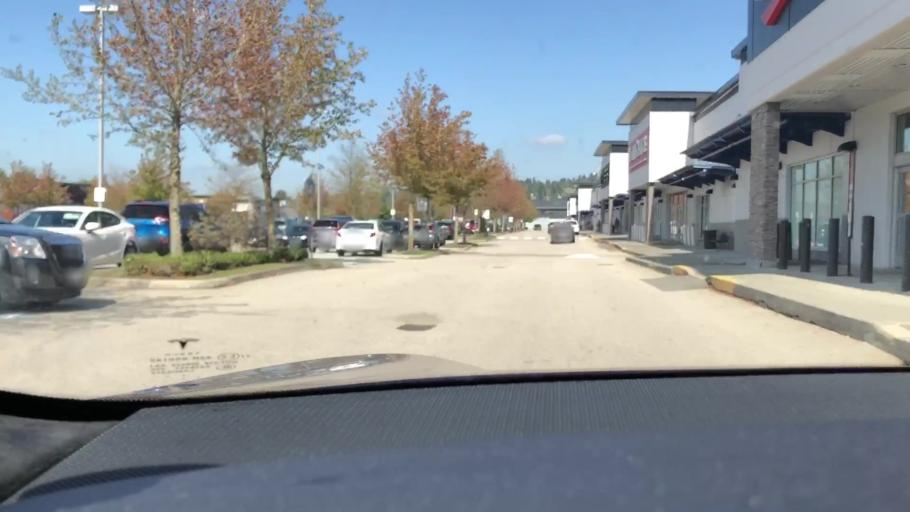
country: CA
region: British Columbia
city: New Westminster
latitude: 49.1986
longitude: -122.9753
